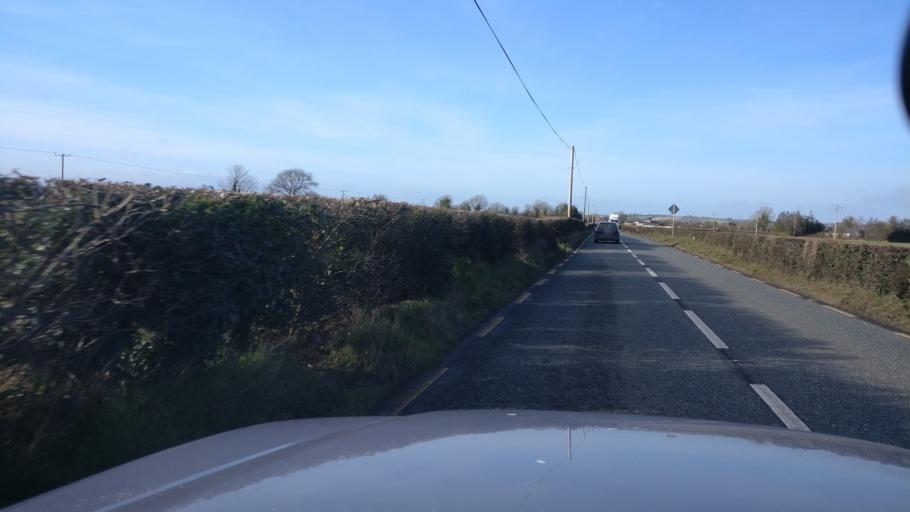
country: IE
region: Leinster
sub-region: Laois
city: Mountmellick
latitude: 53.1664
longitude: -7.3753
